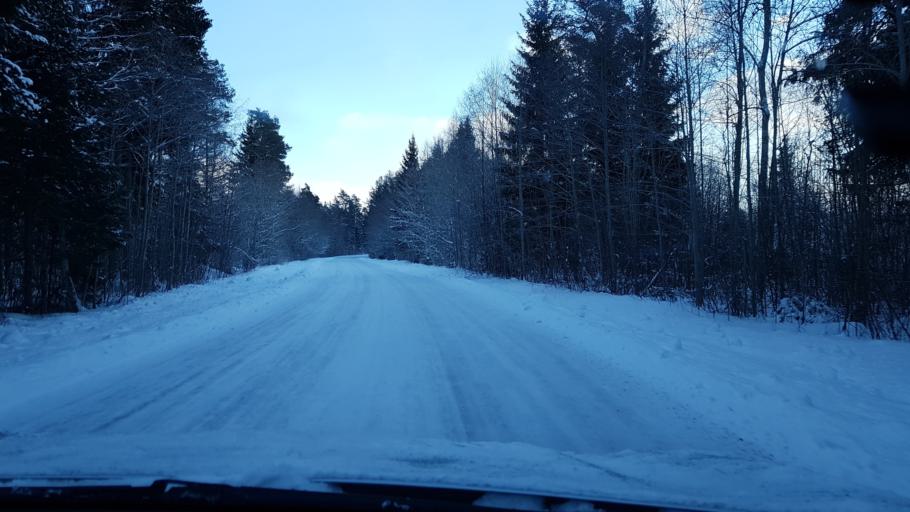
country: EE
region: Harju
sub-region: Nissi vald
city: Turba
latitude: 59.1454
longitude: 24.1539
